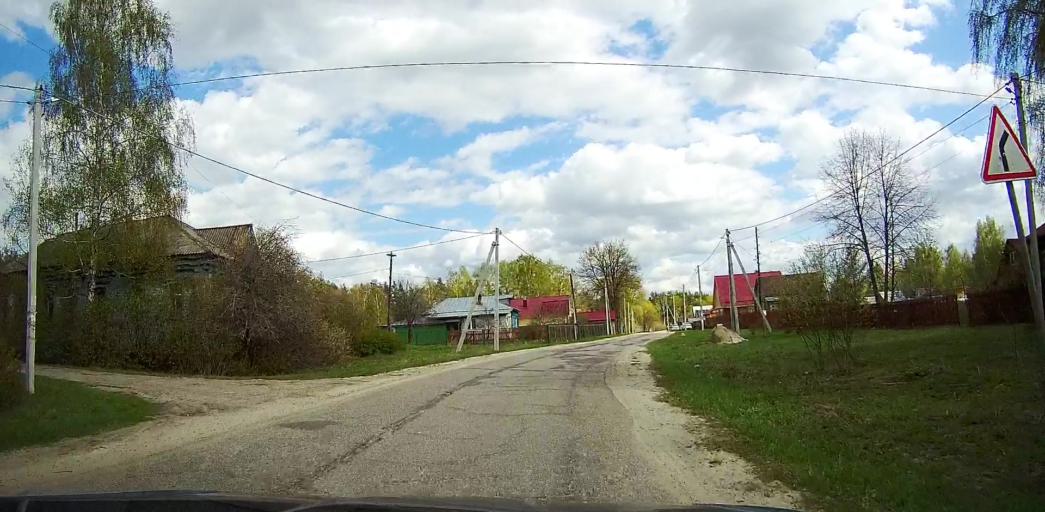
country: RU
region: Moskovskaya
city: Davydovo
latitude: 55.6475
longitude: 38.7633
